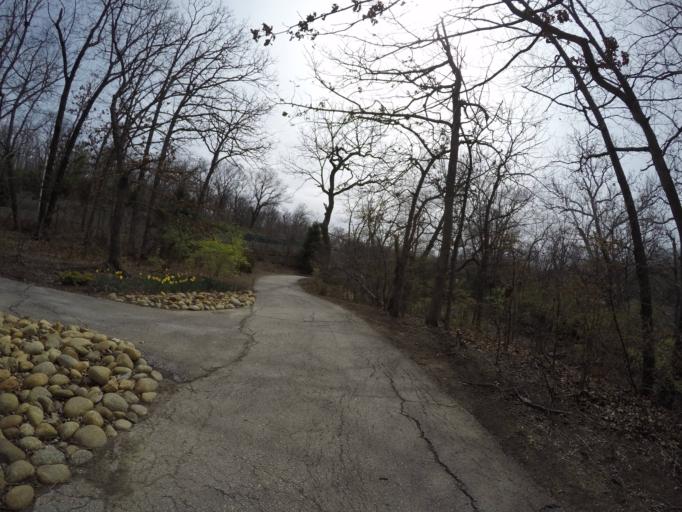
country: US
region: Kansas
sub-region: Johnson County
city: Leawood
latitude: 38.9289
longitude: -94.6218
